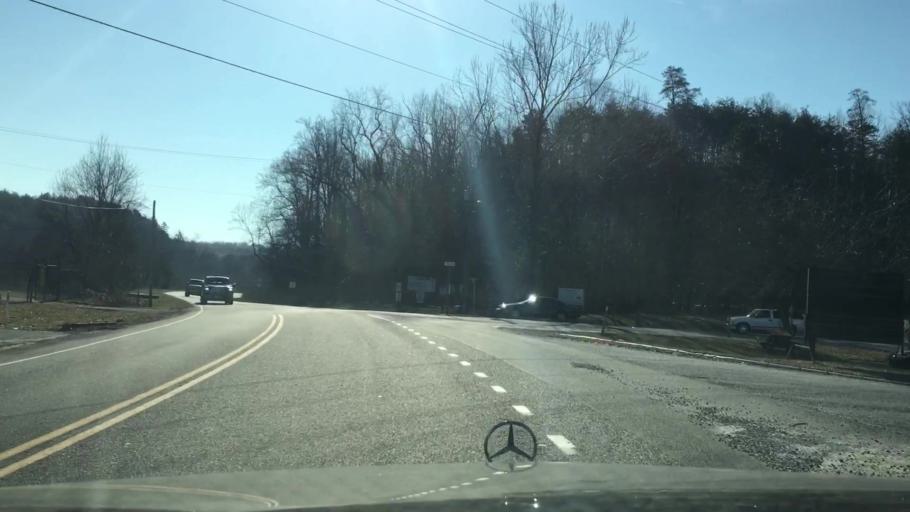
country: US
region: Virginia
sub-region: Campbell County
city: Altavista
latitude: 37.1032
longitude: -79.2847
